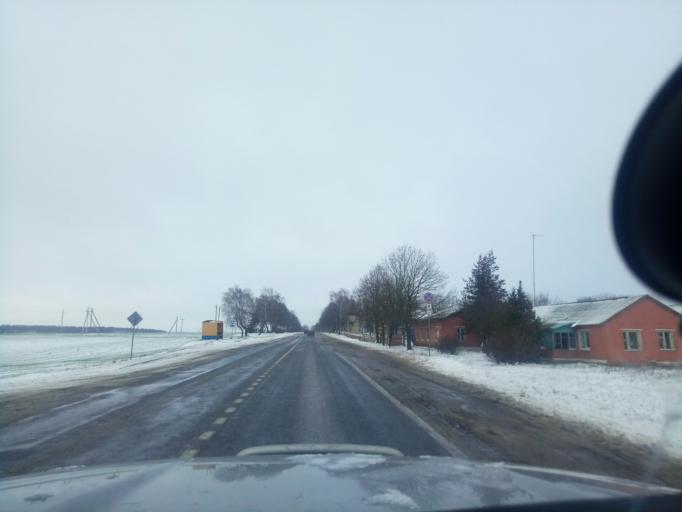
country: BY
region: Minsk
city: Tsimkavichy
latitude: 53.0857
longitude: 27.0180
